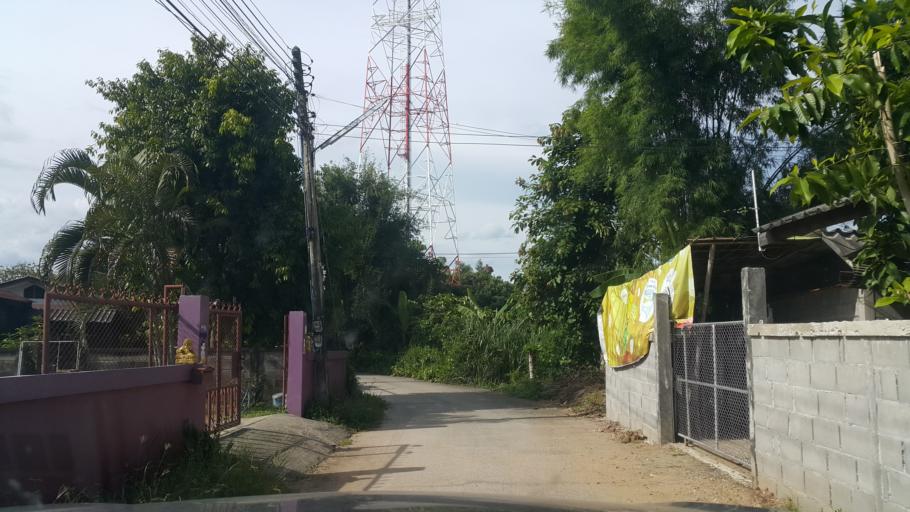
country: TH
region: Chiang Mai
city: San Kamphaeng
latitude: 18.8197
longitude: 99.1235
